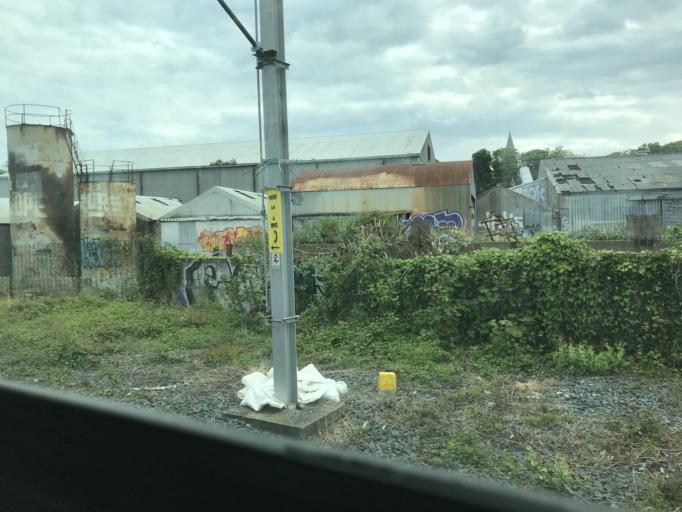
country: IE
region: Leinster
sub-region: Fingal County
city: Howth
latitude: 53.3898
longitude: -6.0789
